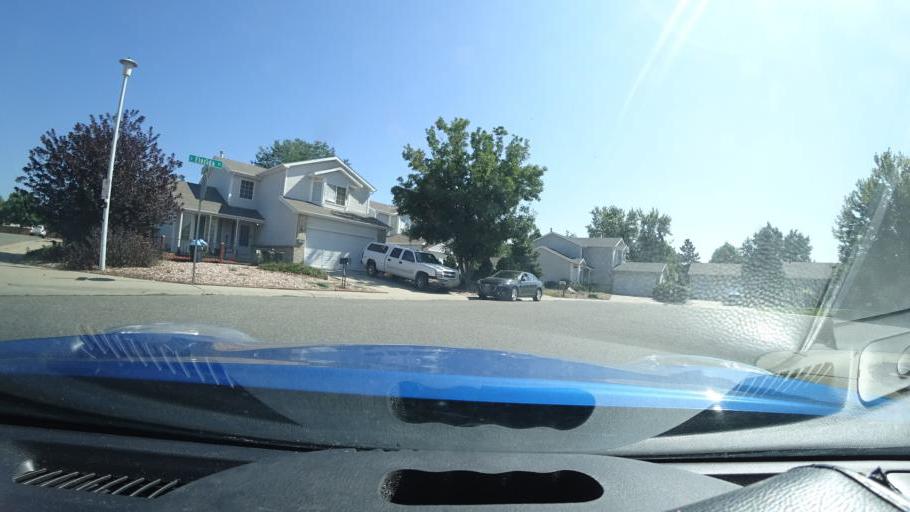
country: US
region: Colorado
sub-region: Adams County
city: Aurora
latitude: 39.6885
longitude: -104.8235
